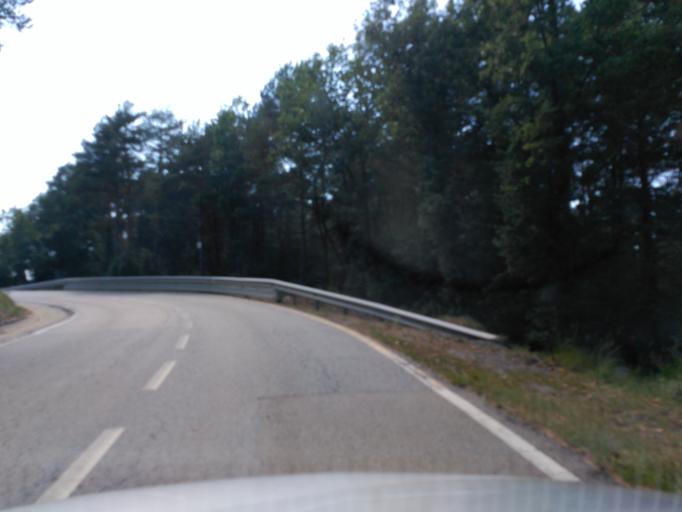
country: ES
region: Catalonia
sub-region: Provincia de Barcelona
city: Orista
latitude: 41.8946
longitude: 2.1053
